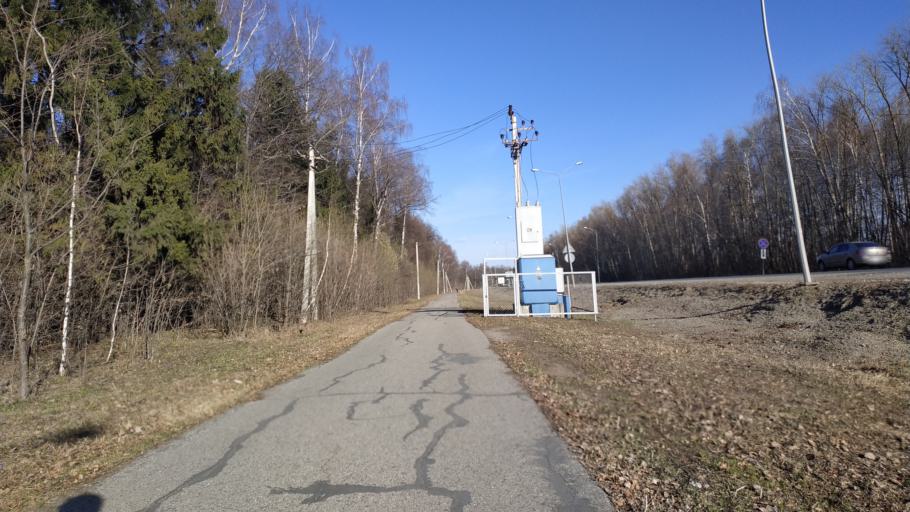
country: RU
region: Chuvashia
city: Ishley
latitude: 56.1339
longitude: 47.1023
